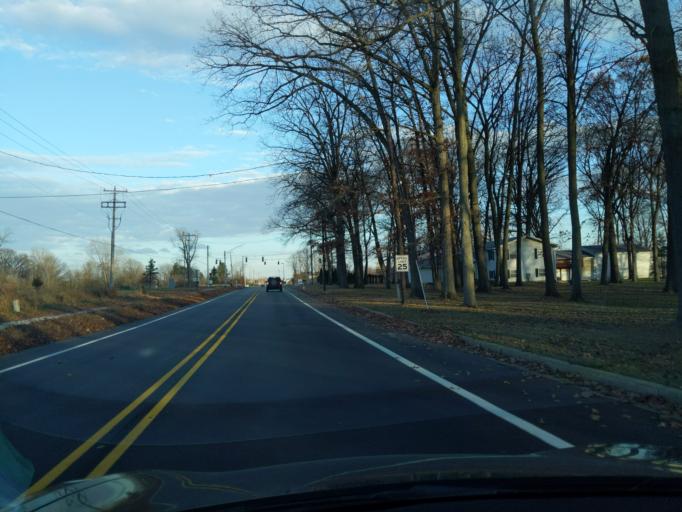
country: US
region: Michigan
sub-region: Ingham County
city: East Lansing
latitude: 42.7732
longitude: -84.5049
